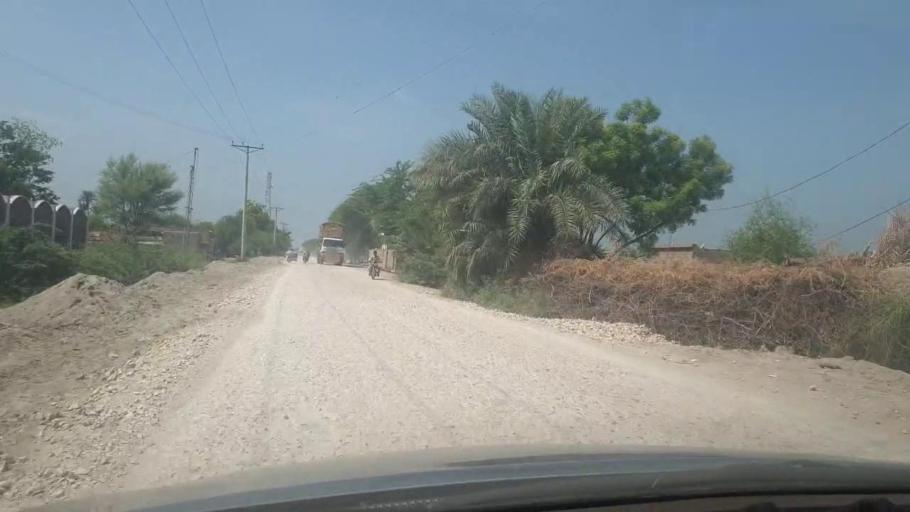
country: PK
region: Sindh
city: Ranipur
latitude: 27.2837
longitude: 68.6022
